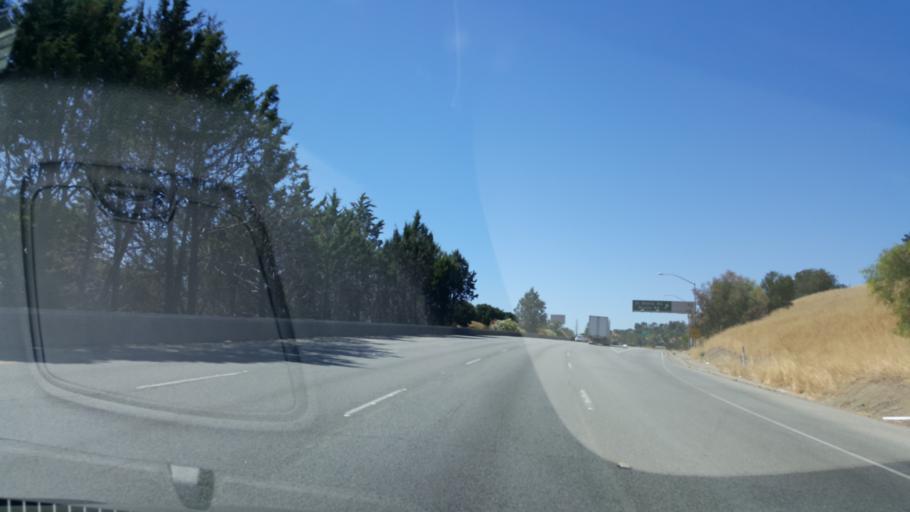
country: US
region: California
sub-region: Santa Clara County
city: Loyola
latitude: 37.3573
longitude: -122.1170
